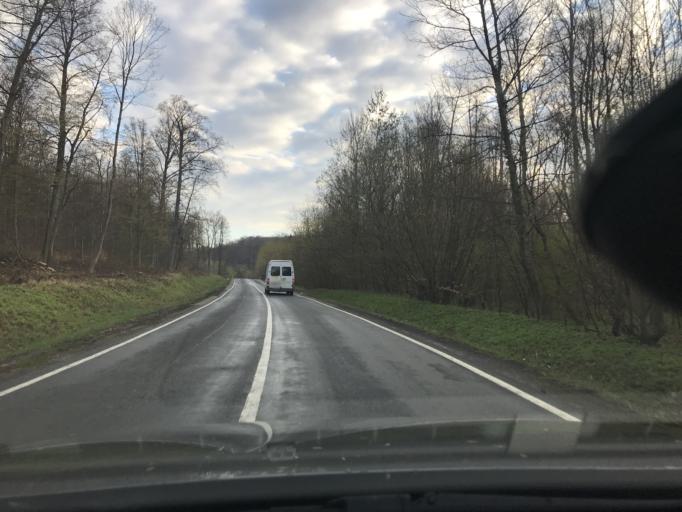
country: DE
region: Thuringia
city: Menteroda
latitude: 51.2882
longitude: 10.5497
